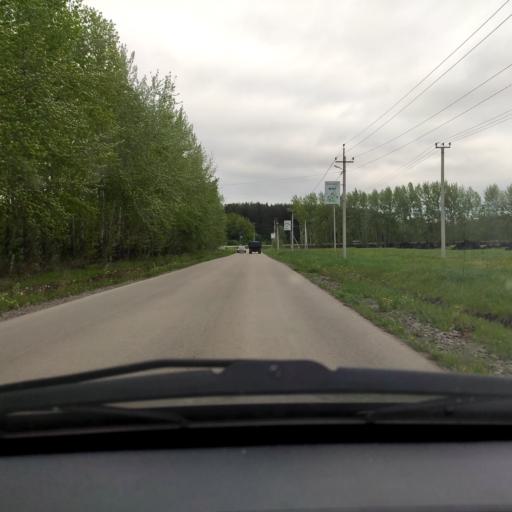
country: RU
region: Bashkortostan
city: Kabakovo
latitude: 54.6155
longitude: 56.1586
